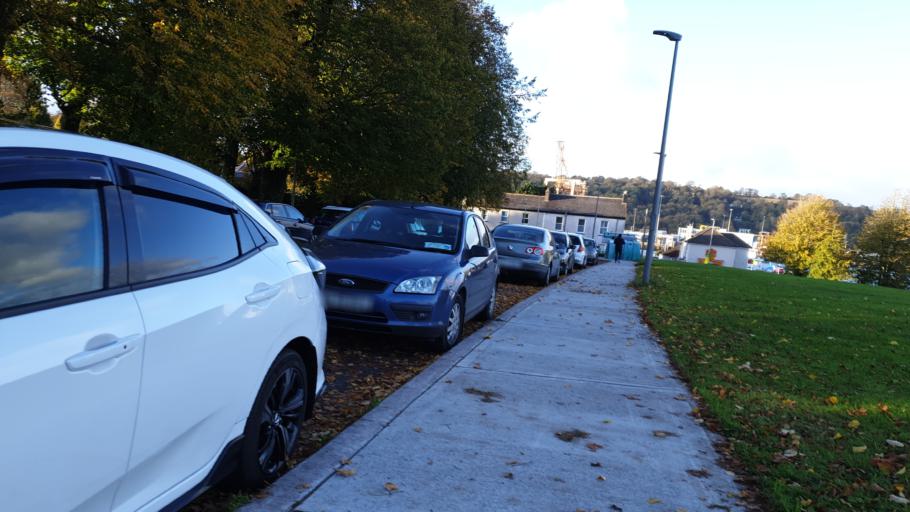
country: IE
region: Munster
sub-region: County Cork
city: Cork
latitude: 51.8963
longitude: -8.4134
